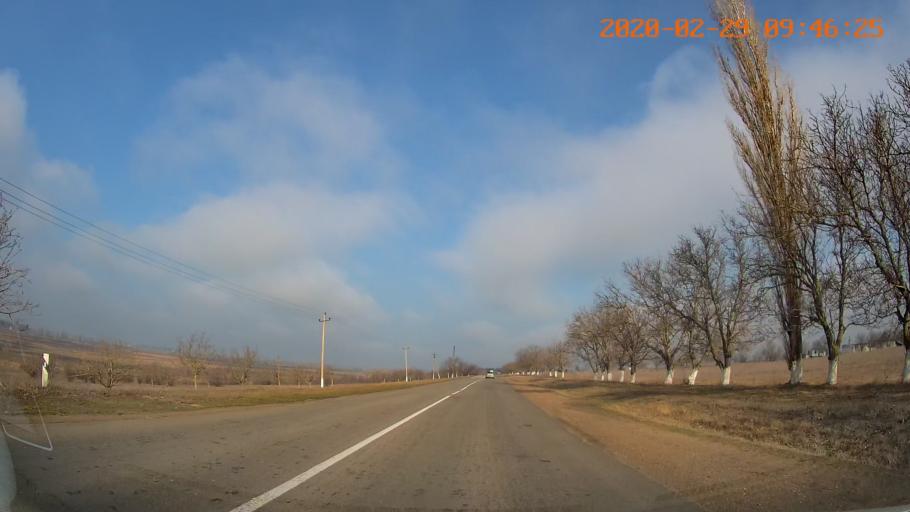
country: MD
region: Telenesti
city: Crasnoe
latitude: 46.6666
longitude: 29.7987
